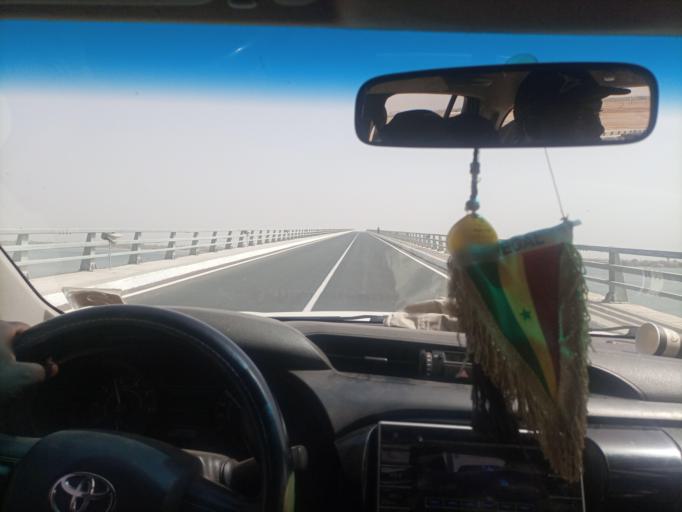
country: SN
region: Fatick
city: Foundiougne
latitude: 14.1409
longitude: -16.4710
